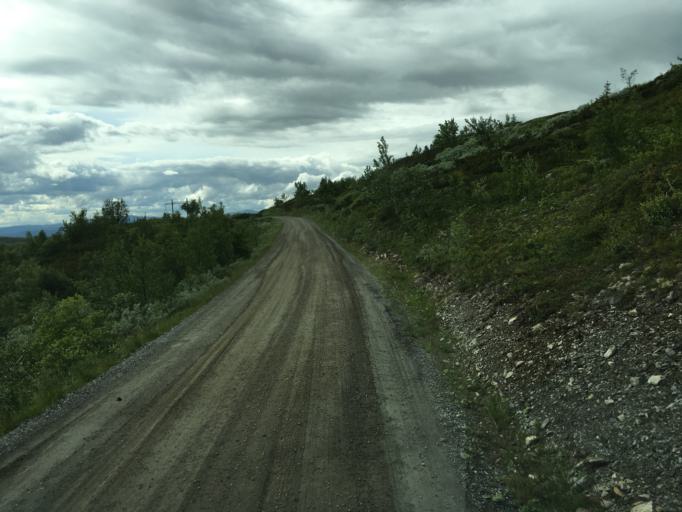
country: NO
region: Oppland
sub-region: Ringebu
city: Ringebu
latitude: 61.3638
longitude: 10.0324
